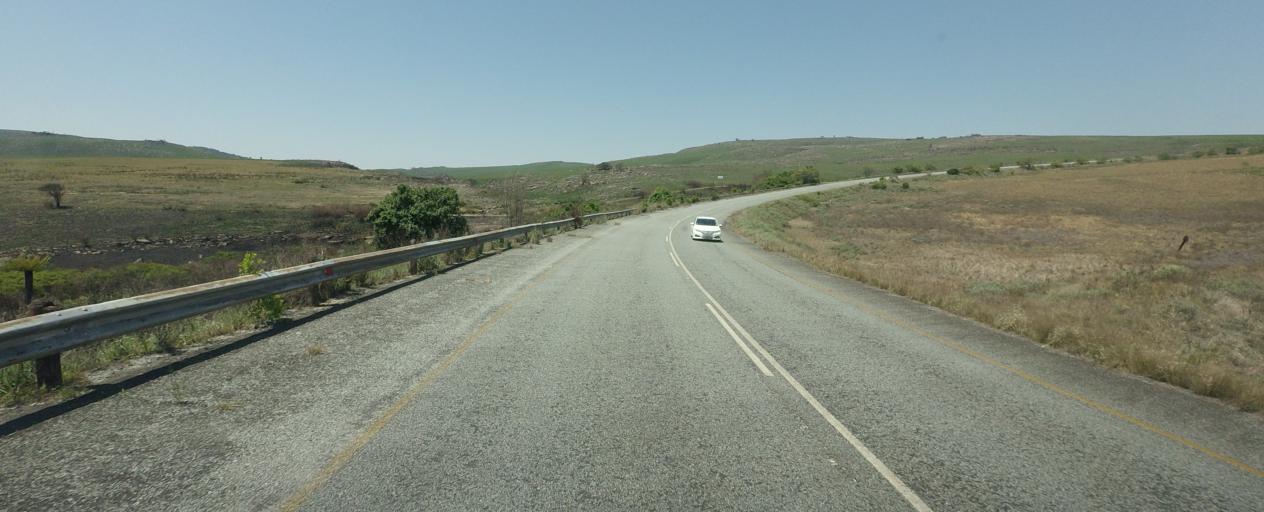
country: ZA
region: Mpumalanga
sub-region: Ehlanzeni District
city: Graksop
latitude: -24.8541
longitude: 30.8881
